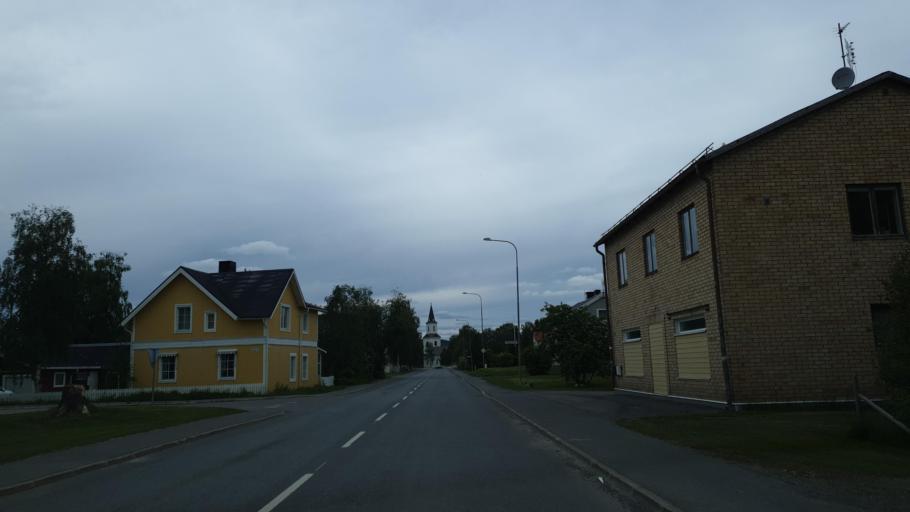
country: SE
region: Vaesterbotten
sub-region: Sorsele Kommun
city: Sorsele
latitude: 65.5395
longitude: 17.5219
